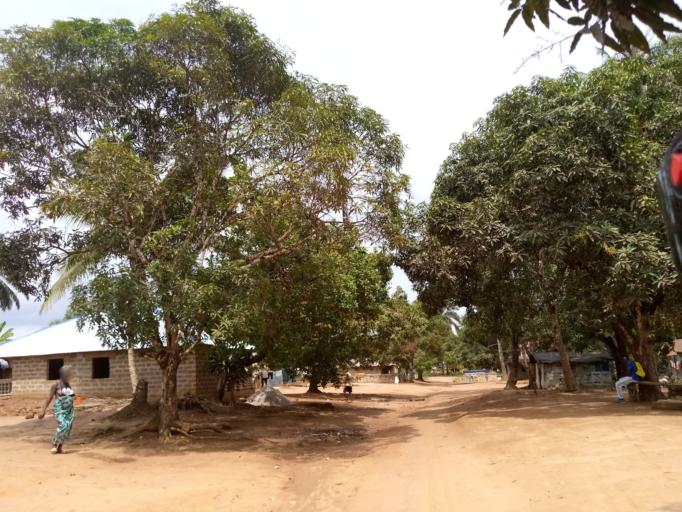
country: SL
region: Western Area
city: Waterloo
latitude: 8.3261
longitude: -13.0140
